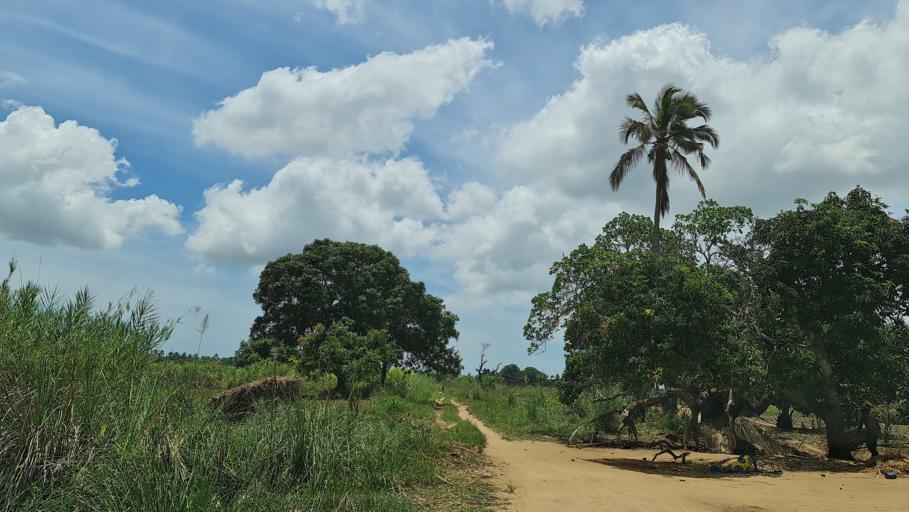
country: MZ
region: Zambezia
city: Quelimane
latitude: -17.5798
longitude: 37.3747
